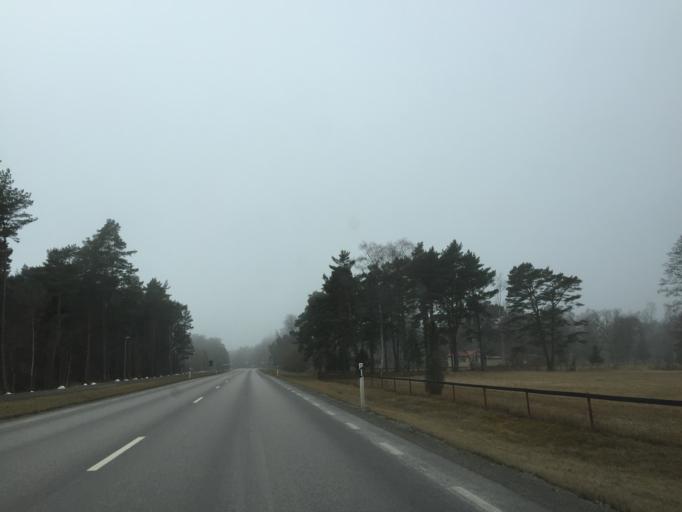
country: EE
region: Saare
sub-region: Kuressaare linn
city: Kuressaare
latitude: 58.2161
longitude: 22.3234
